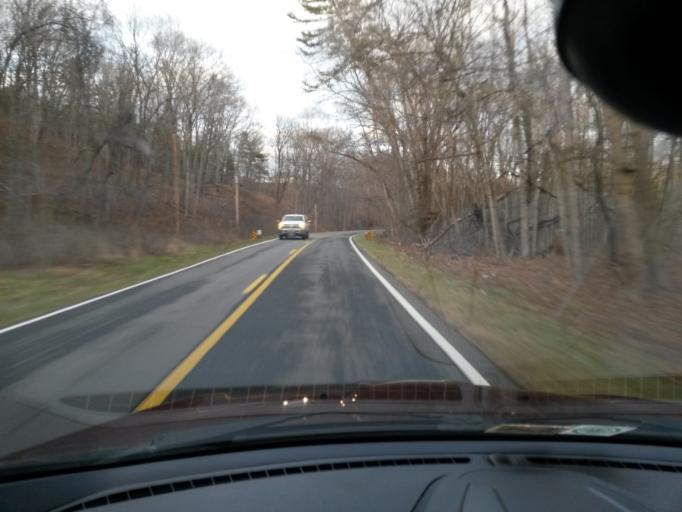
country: US
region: Virginia
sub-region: City of Covington
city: Covington
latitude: 37.7801
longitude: -80.1073
